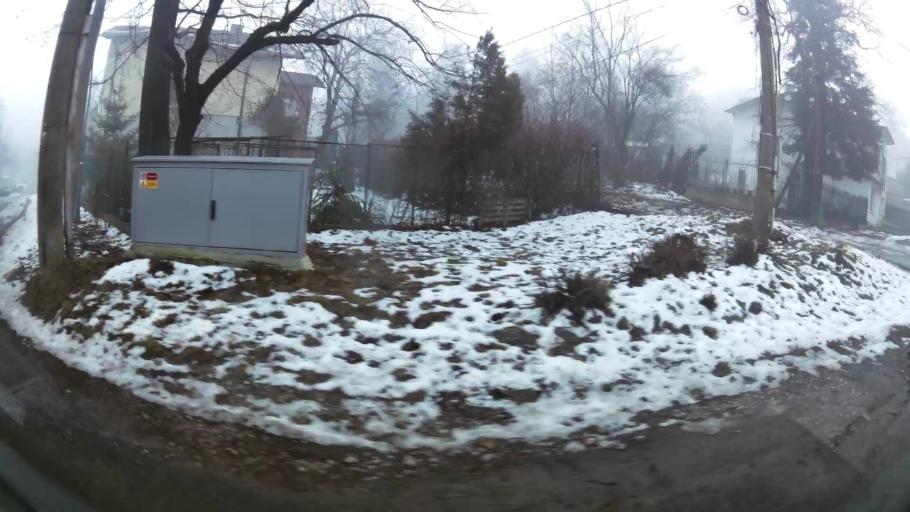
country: BG
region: Sofia-Capital
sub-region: Stolichna Obshtina
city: Sofia
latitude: 42.6602
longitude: 23.2502
